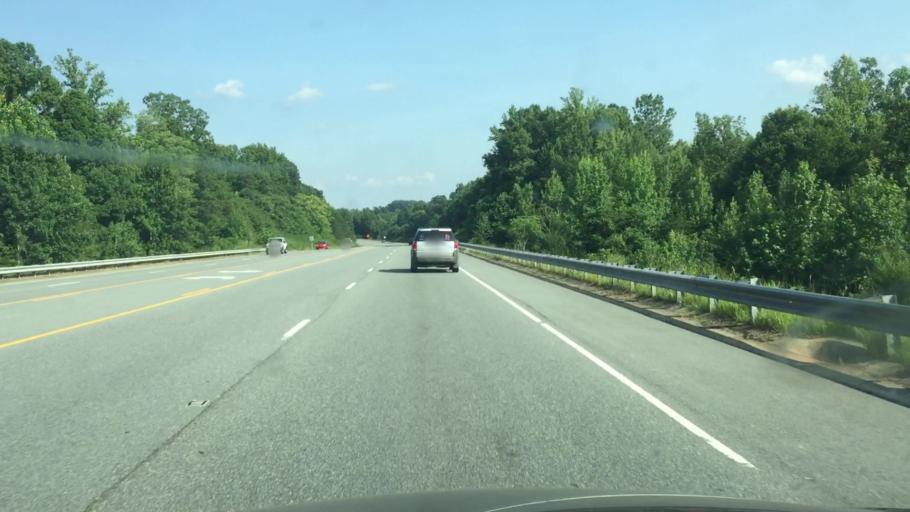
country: US
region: North Carolina
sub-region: Rockingham County
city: Reidsville
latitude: 36.3675
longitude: -79.6434
